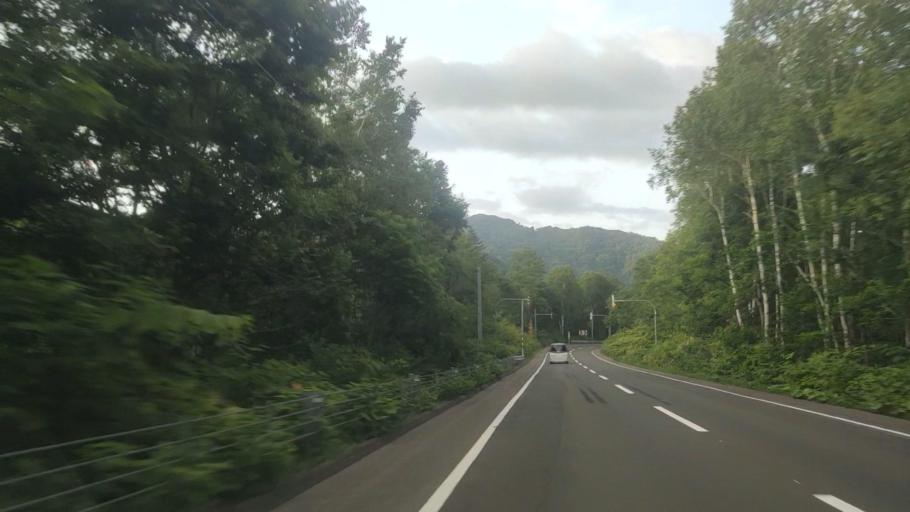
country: JP
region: Hokkaido
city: Ashibetsu
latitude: 43.3018
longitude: 142.1138
